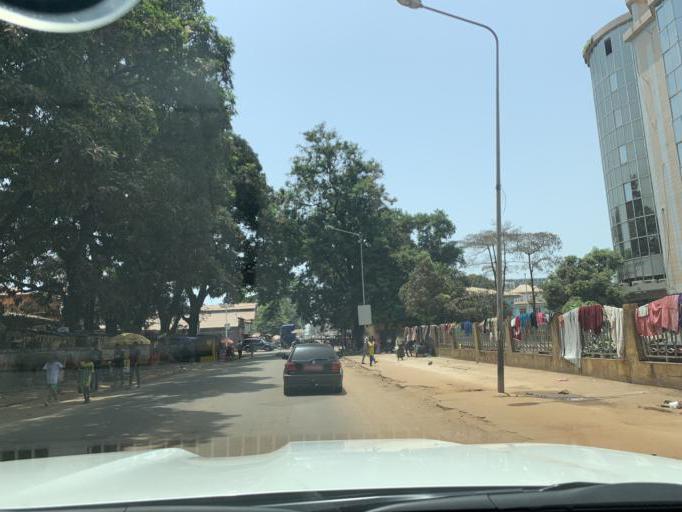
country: GN
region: Conakry
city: Camayenne
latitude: 9.5144
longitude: -13.7060
